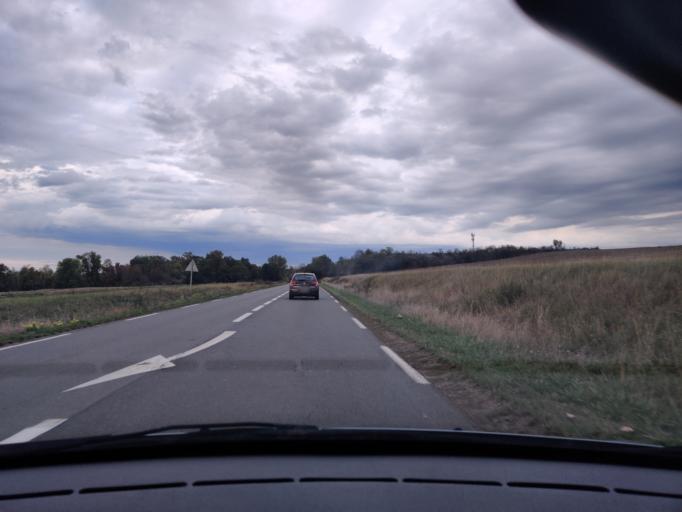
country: FR
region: Auvergne
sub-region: Departement du Puy-de-Dome
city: Riom
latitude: 45.9123
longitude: 3.1219
